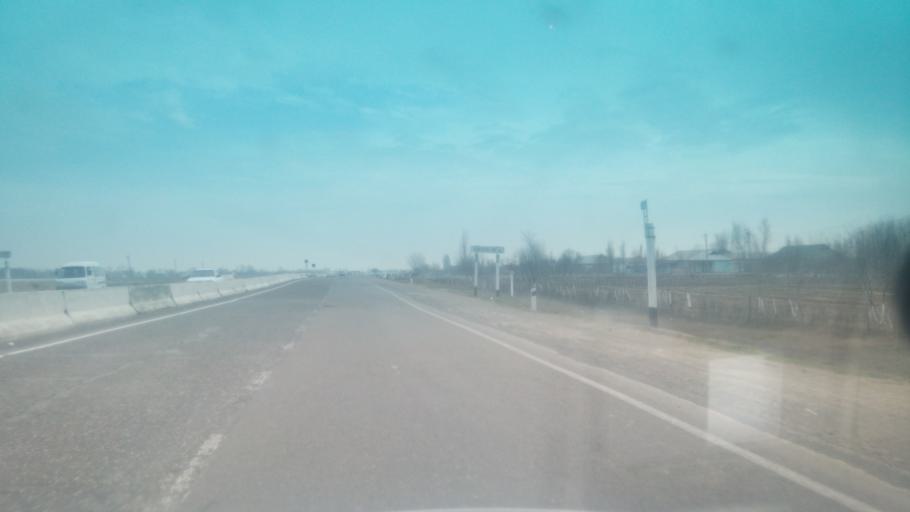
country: KZ
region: Ongtustik Qazaqstan
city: Myrzakent
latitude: 40.5085
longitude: 68.5051
